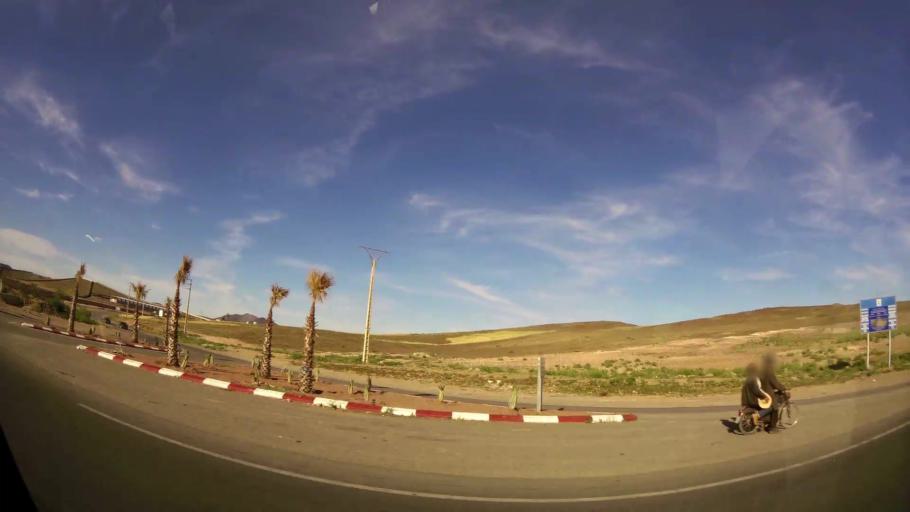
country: MA
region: Marrakech-Tensift-Al Haouz
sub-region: Marrakech
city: Marrakesh
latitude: 31.7045
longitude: -8.0630
